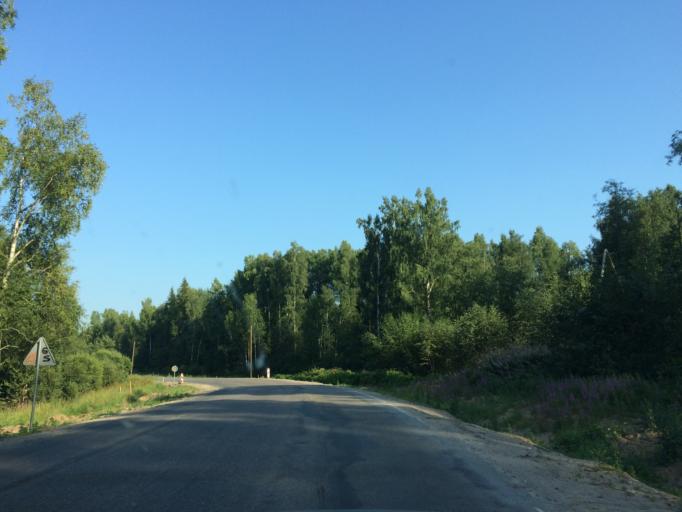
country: LV
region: Rezekne
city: Rezekne
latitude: 56.5138
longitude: 27.4734
